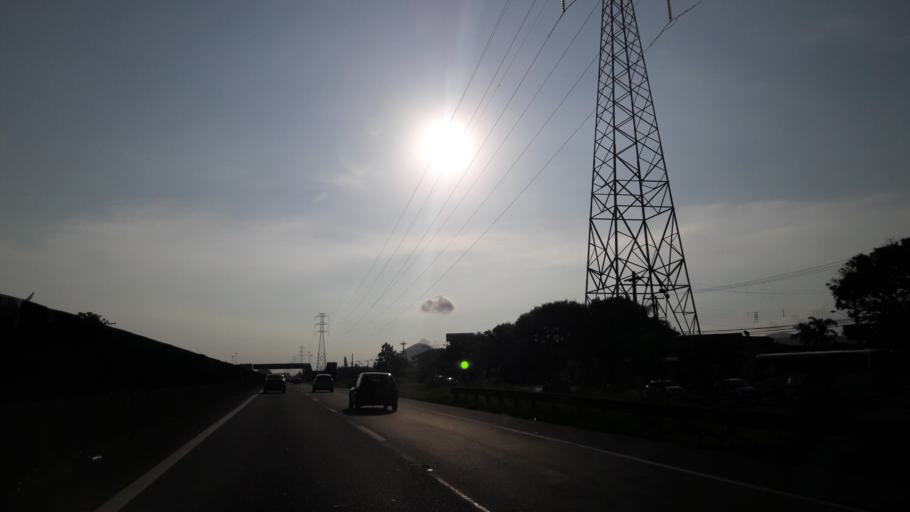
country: BR
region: Sao Paulo
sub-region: Mongagua
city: Mongagua
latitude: -24.1047
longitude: -46.6440
